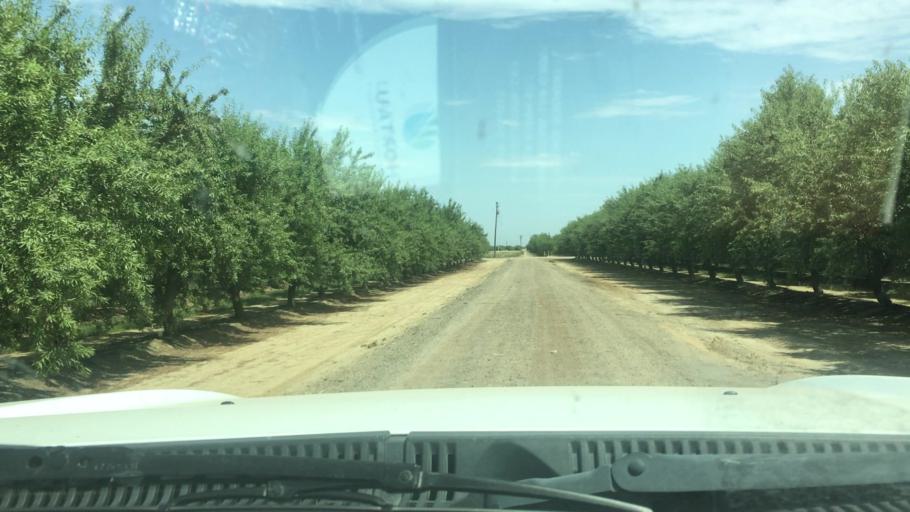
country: US
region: California
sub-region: Kern County
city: Wasco
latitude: 35.5562
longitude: -119.4296
